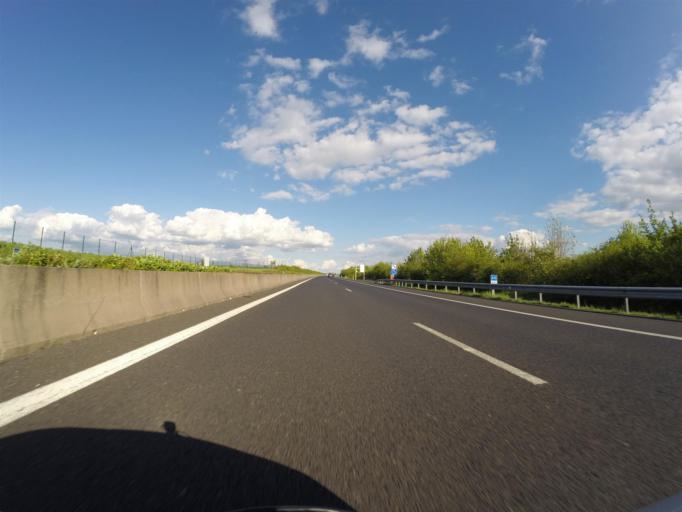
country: LU
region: Grevenmacher
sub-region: Canton de Remich
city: Mondorf-les-Bains
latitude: 49.4940
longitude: 6.3202
